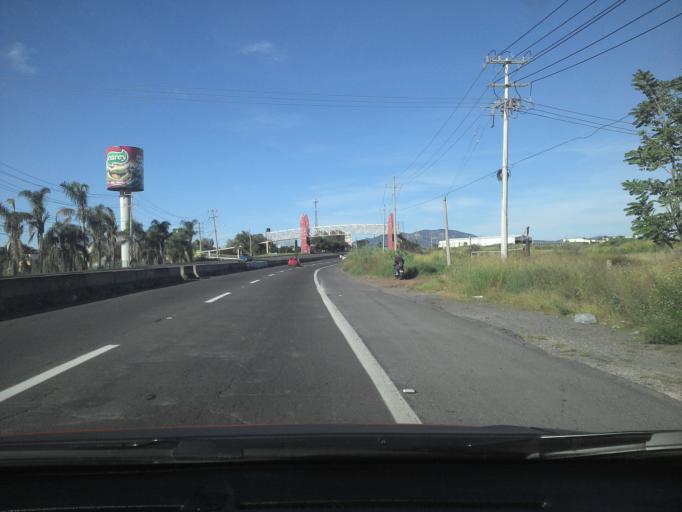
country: MX
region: Jalisco
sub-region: Tala
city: Los Ruisenores
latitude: 20.7012
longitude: -103.6884
